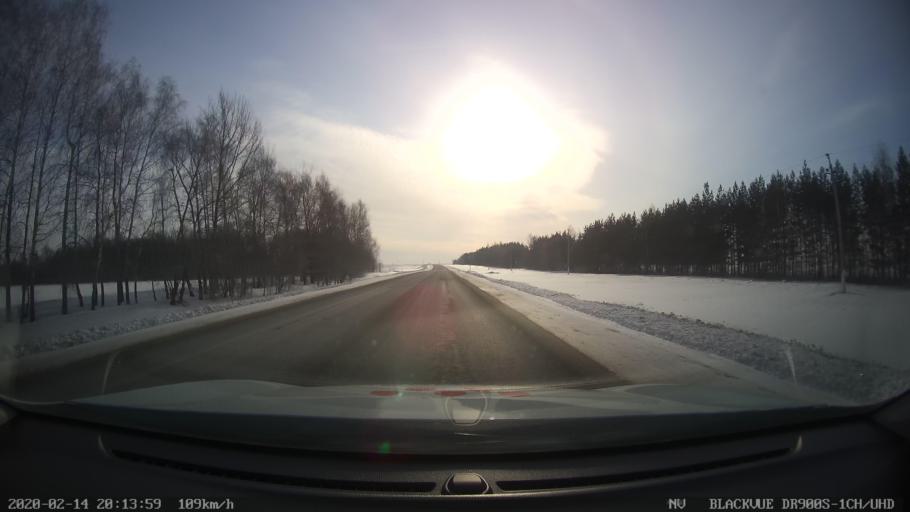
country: RU
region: Tatarstan
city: Verkhniy Uslon
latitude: 55.6507
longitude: 48.8673
